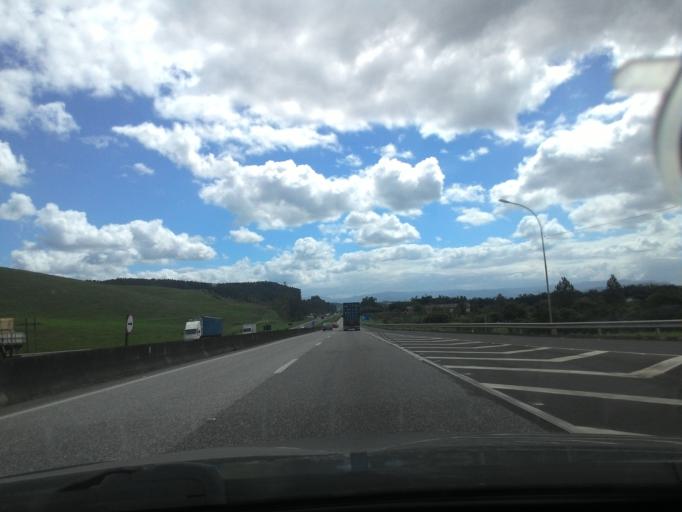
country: BR
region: Sao Paulo
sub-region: Jacupiranga
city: Jacupiranga
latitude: -24.7101
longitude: -48.0203
